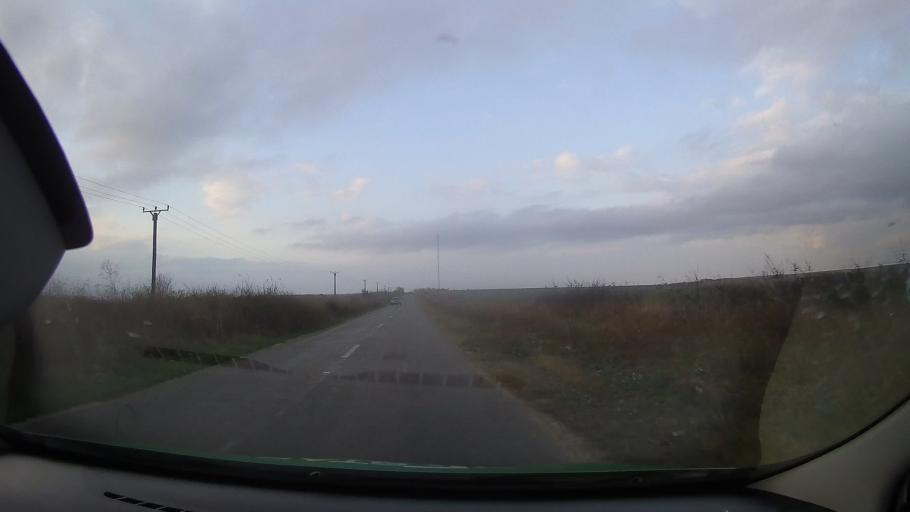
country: RO
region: Constanta
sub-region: Comuna Dobromir
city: Dobromir
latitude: 44.0390
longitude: 27.7577
